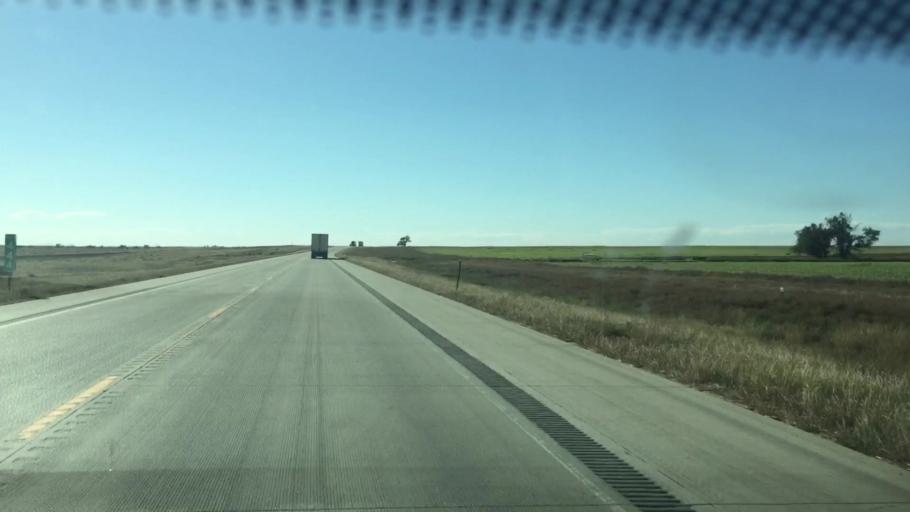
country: US
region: Colorado
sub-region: Kiowa County
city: Eads
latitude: 38.7639
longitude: -102.8169
